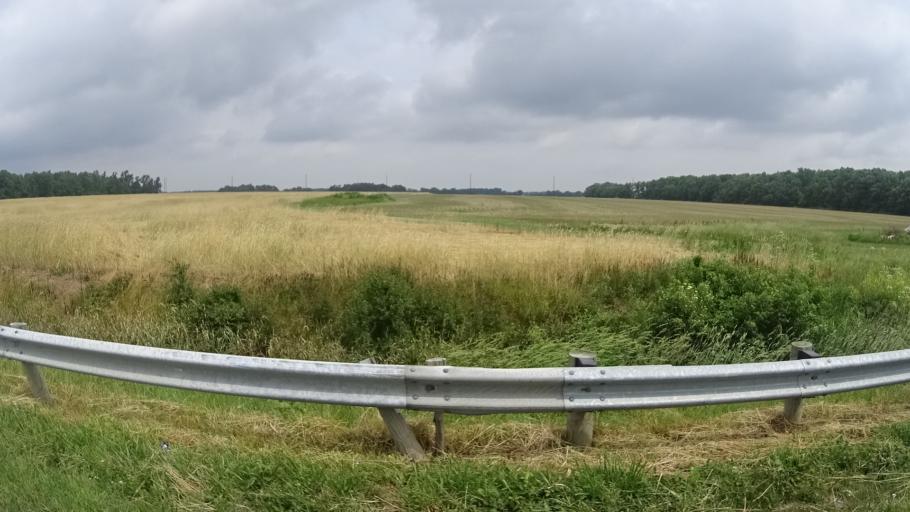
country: US
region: Ohio
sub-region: Huron County
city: Bellevue
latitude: 41.3258
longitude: -82.8119
